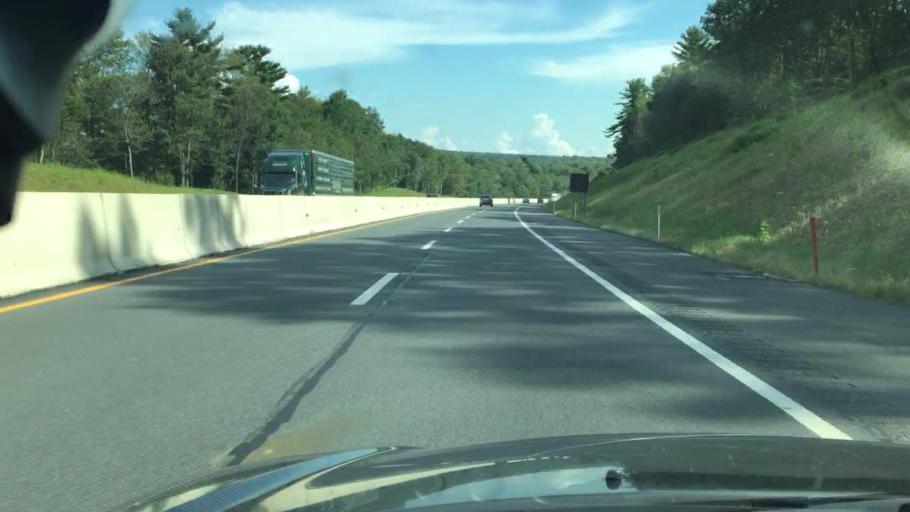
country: US
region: Pennsylvania
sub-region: Carbon County
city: Towamensing Trails
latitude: 41.0133
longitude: -75.6388
